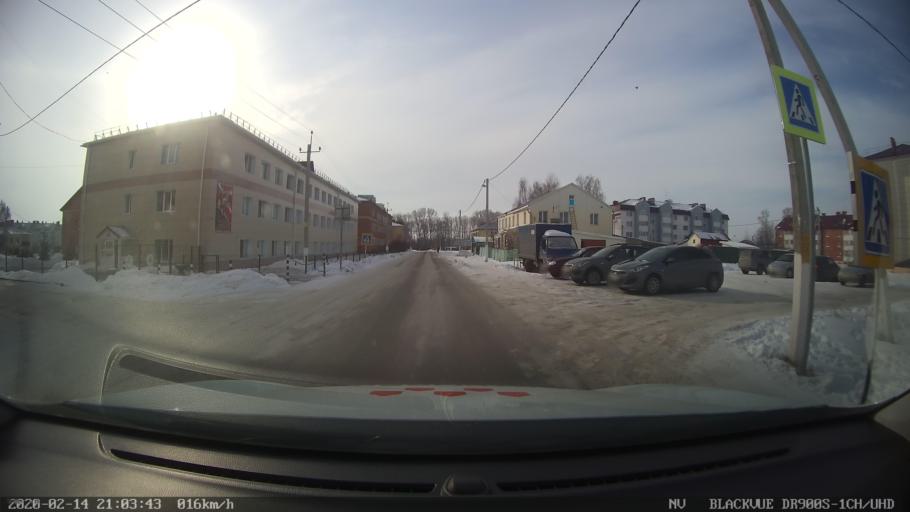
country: RU
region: Tatarstan
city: Kuybyshevskiy Zaton
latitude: 55.1559
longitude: 49.1752
